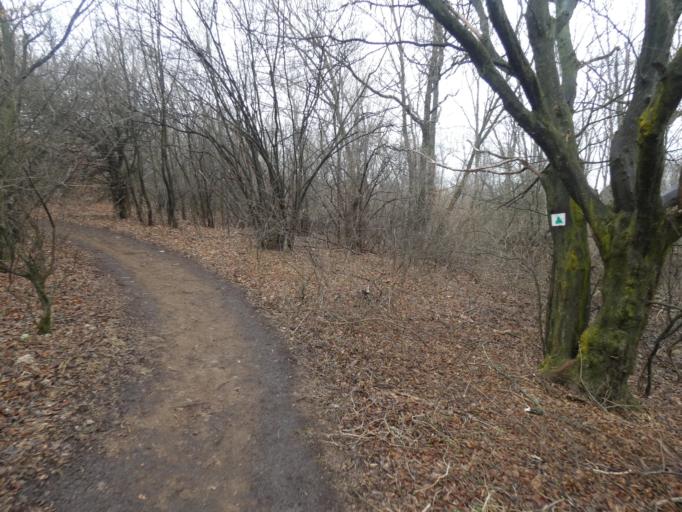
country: HU
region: Pest
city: Telki
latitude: 47.5511
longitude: 18.8664
